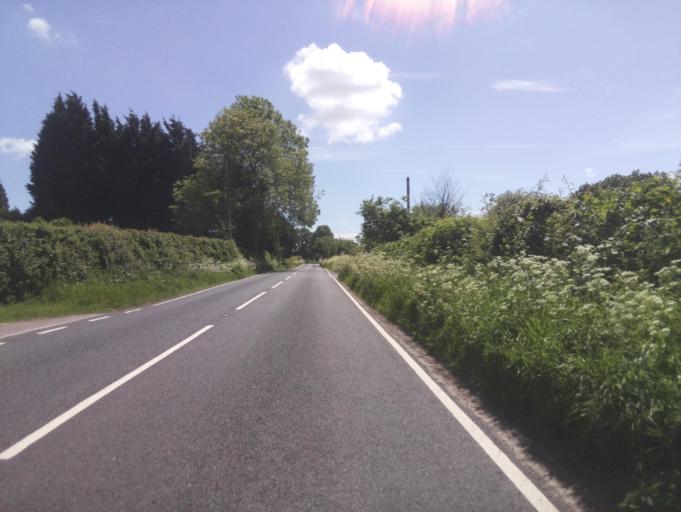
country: GB
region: Wales
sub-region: Monmouthshire
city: Mitchel Troy
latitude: 51.7570
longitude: -2.7226
